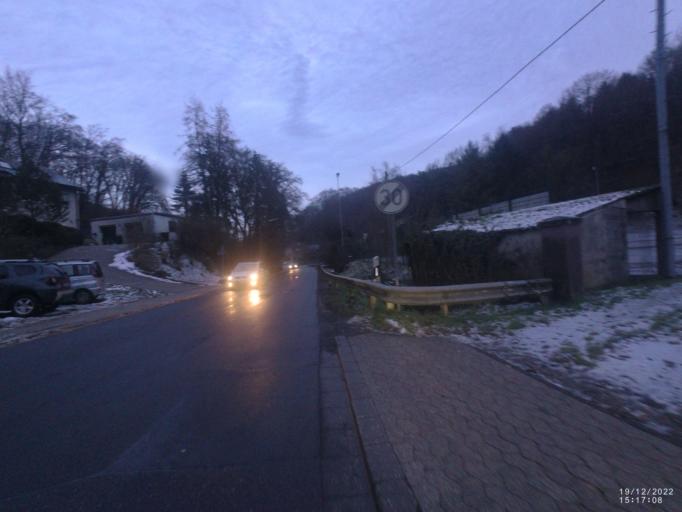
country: DE
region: Rheinland-Pfalz
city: Unkel
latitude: 50.5999
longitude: 7.1988
